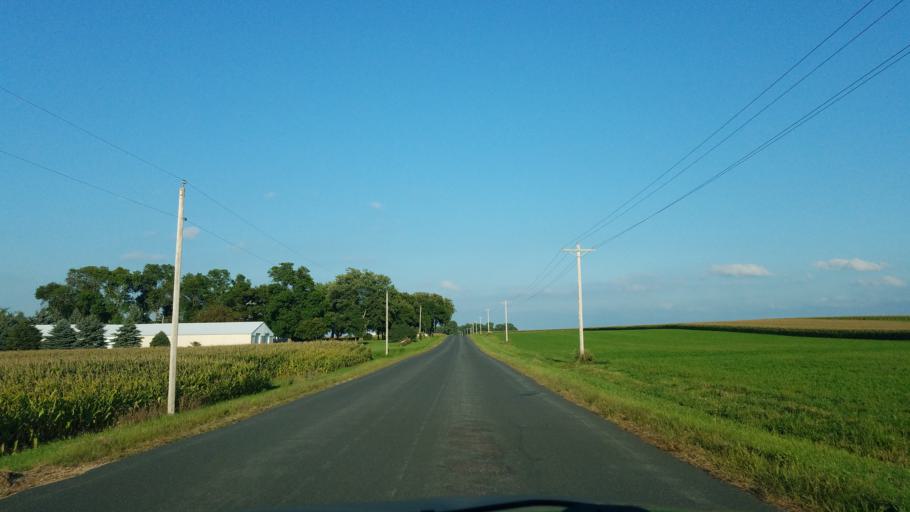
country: US
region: Wisconsin
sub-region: Saint Croix County
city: Roberts
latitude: 45.0071
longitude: -92.5566
